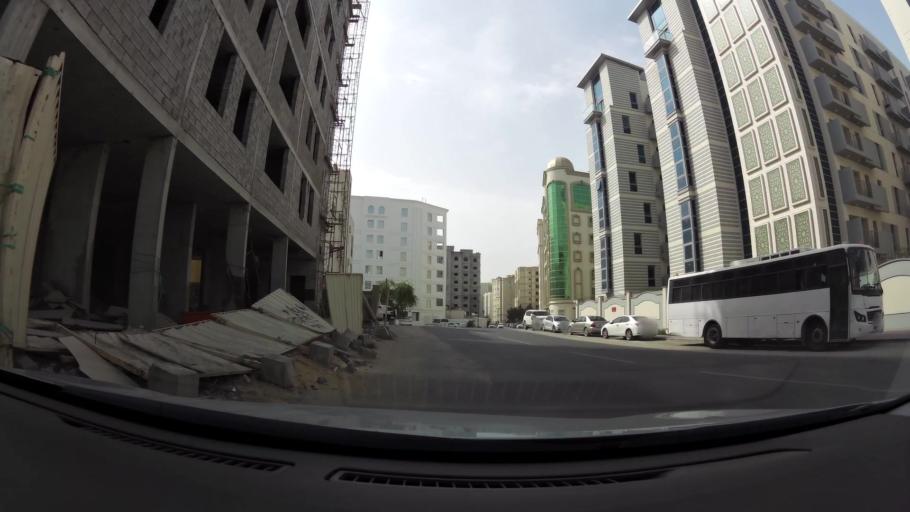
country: QA
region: Baladiyat ad Dawhah
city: Doha
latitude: 25.2835
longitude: 51.5098
